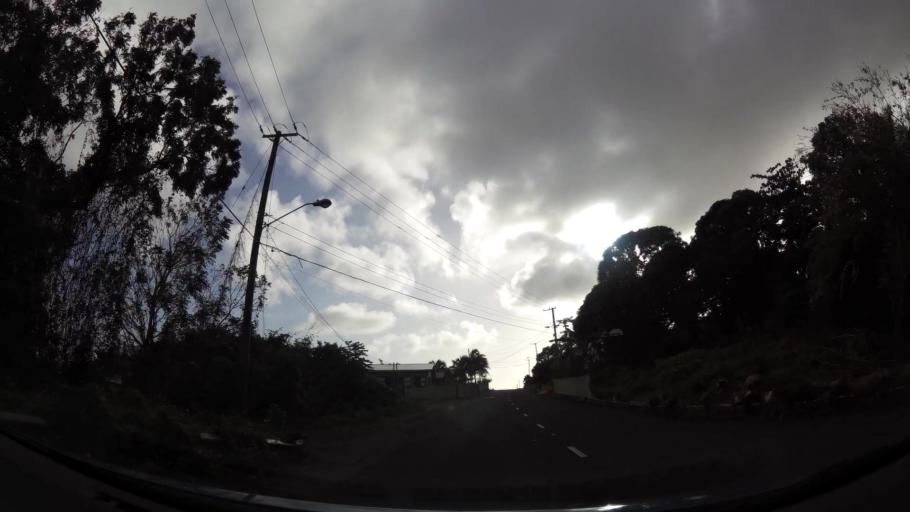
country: KN
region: Saint George Gingerland
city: Market Shop
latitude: 17.1374
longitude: -62.5668
